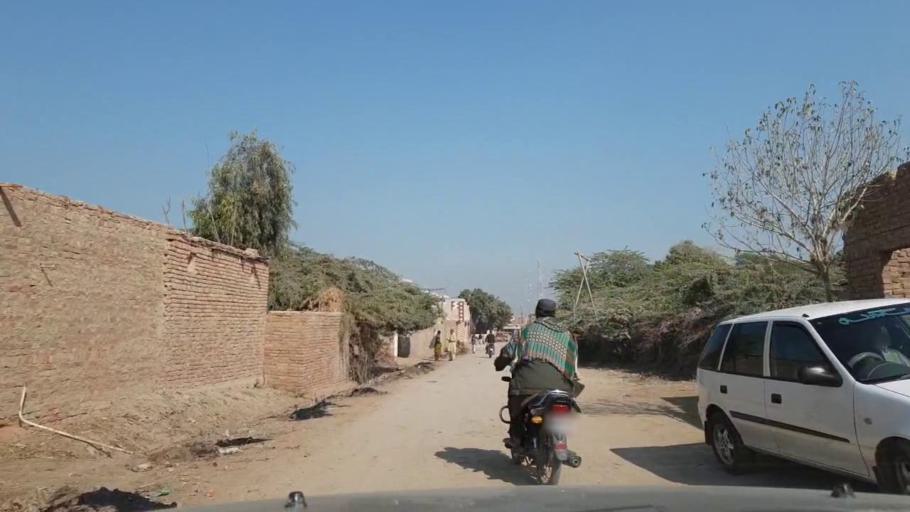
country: PK
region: Sindh
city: Matiari
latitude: 25.6274
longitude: 68.5941
